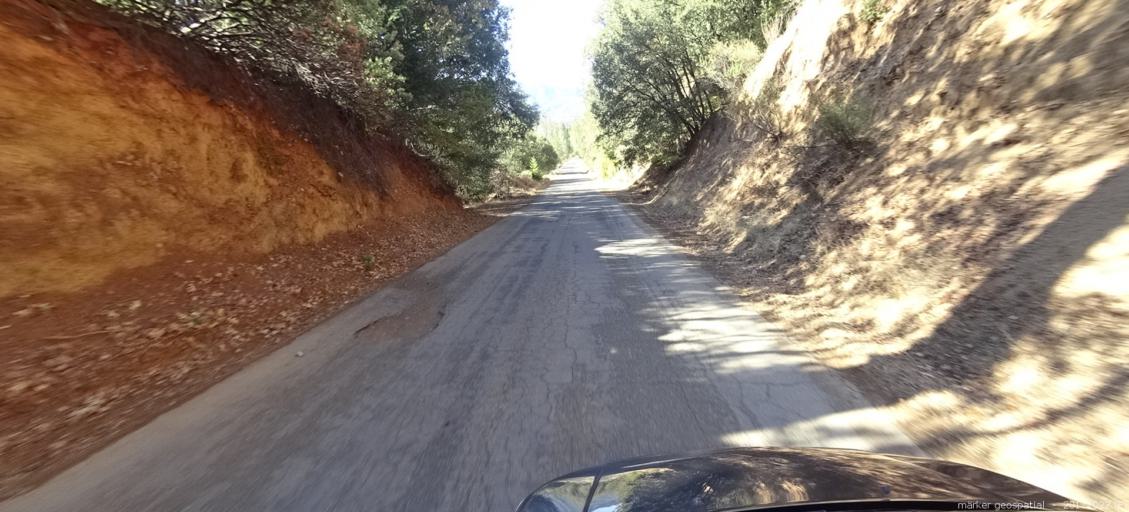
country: US
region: California
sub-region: Shasta County
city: Shasta Lake
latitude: 40.8726
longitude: -122.3609
